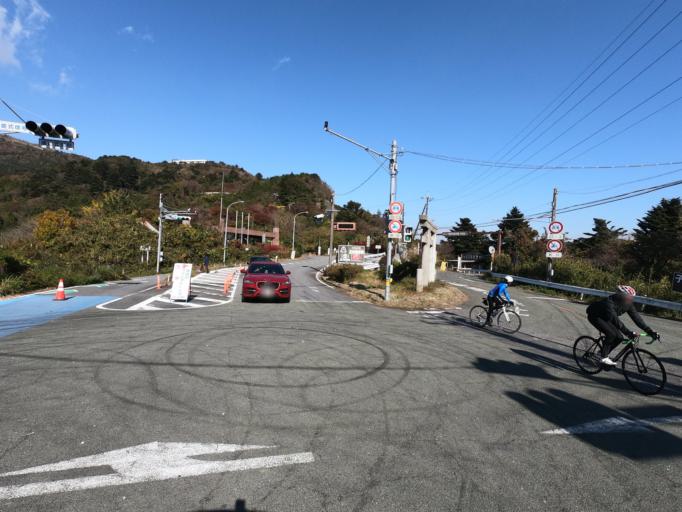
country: JP
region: Ibaraki
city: Tsukuba
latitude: 36.2135
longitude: 140.1222
